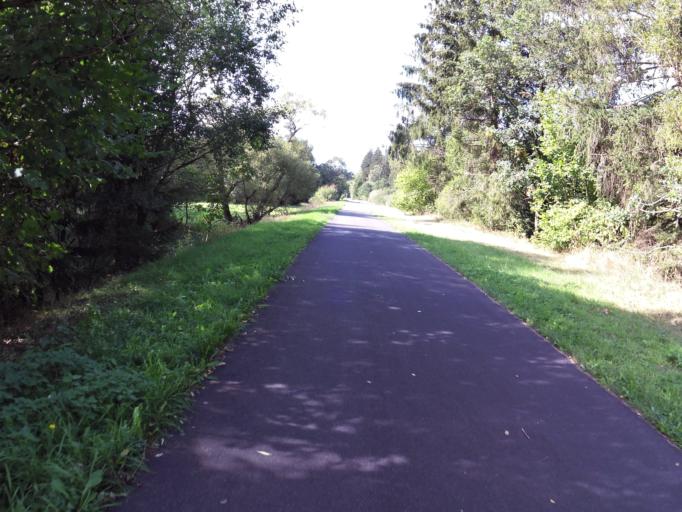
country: DE
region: Rheinland-Pfalz
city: Habscheid
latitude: 50.1912
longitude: 6.2921
